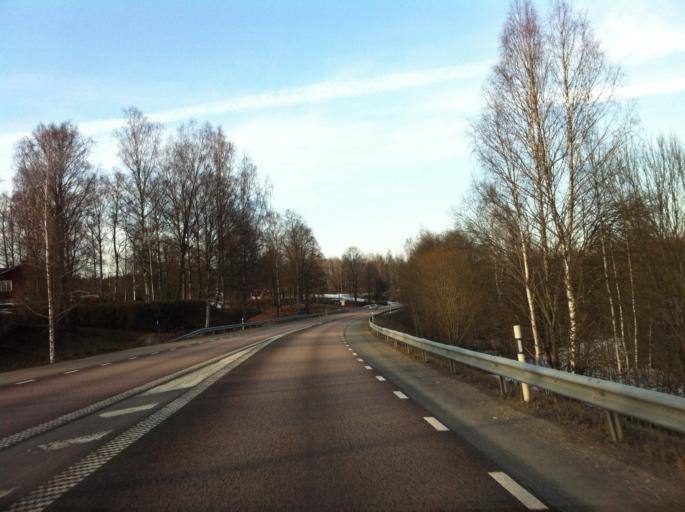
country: SE
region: Vaermland
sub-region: Filipstads Kommun
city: Lesjofors
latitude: 59.8544
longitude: 14.2632
